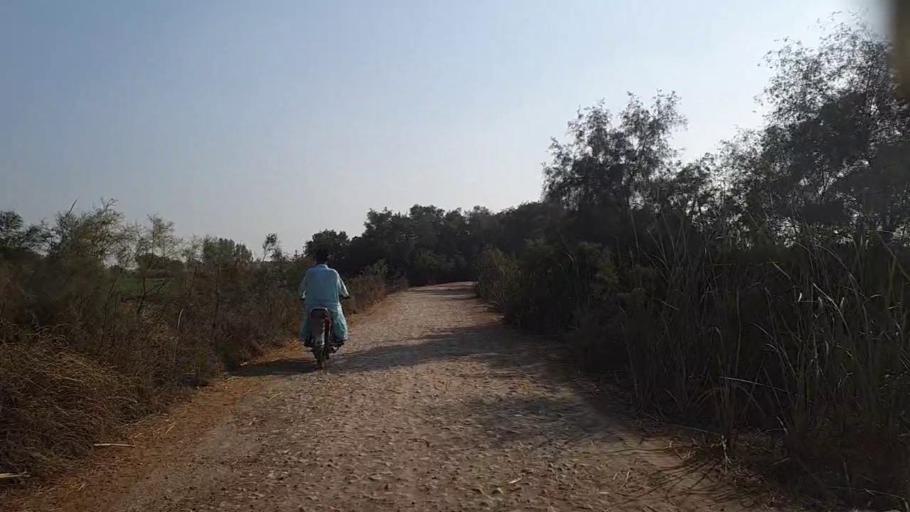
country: PK
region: Sindh
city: Mirpur Mathelo
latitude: 27.8979
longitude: 69.6069
